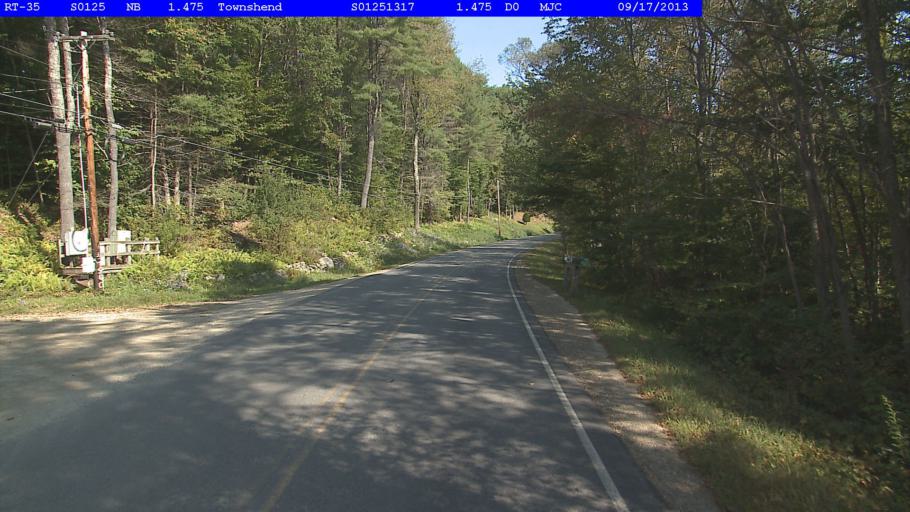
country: US
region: Vermont
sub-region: Windham County
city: Newfane
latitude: 43.0667
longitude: -72.6611
